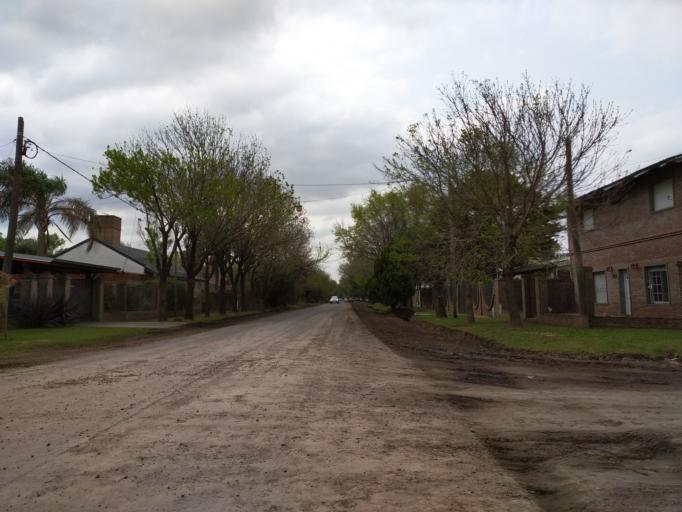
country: AR
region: Santa Fe
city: Funes
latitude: -32.9248
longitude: -60.8510
